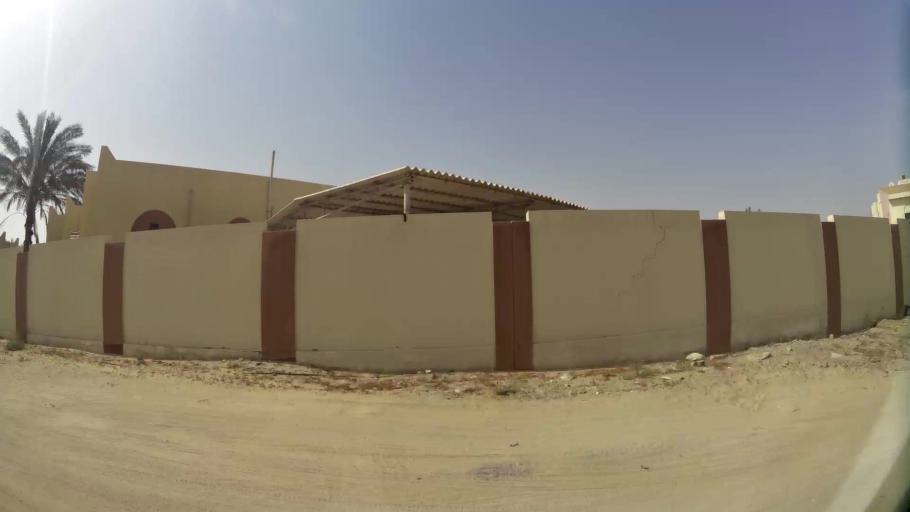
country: AE
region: Ash Shariqah
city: Sharjah
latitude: 25.3493
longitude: 55.4202
